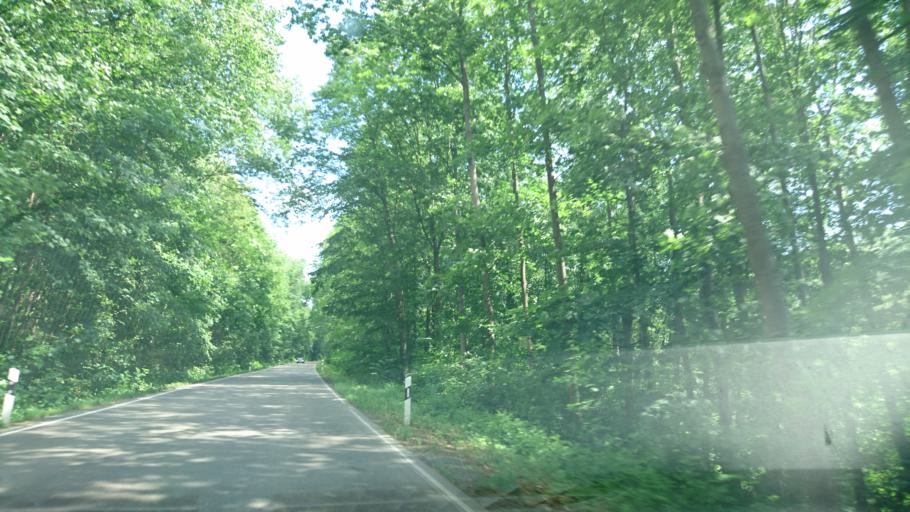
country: DE
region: Saxony
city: Struppen
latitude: 50.9219
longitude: 13.9758
